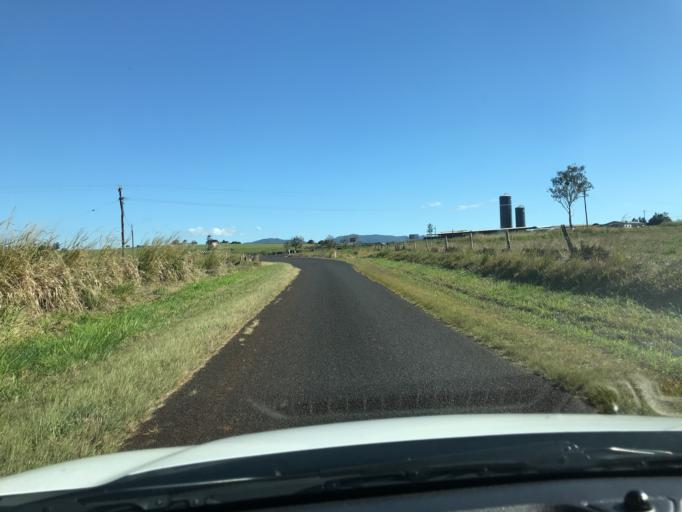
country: AU
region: Queensland
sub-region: Tablelands
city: Atherton
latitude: -17.2968
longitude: 145.5434
